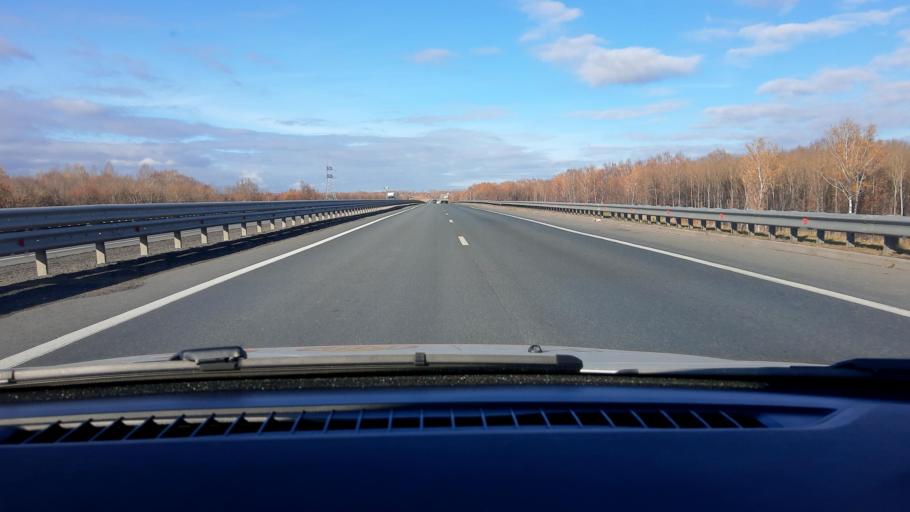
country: RU
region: Nizjnij Novgorod
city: Burevestnik
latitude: 56.1337
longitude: 43.7745
